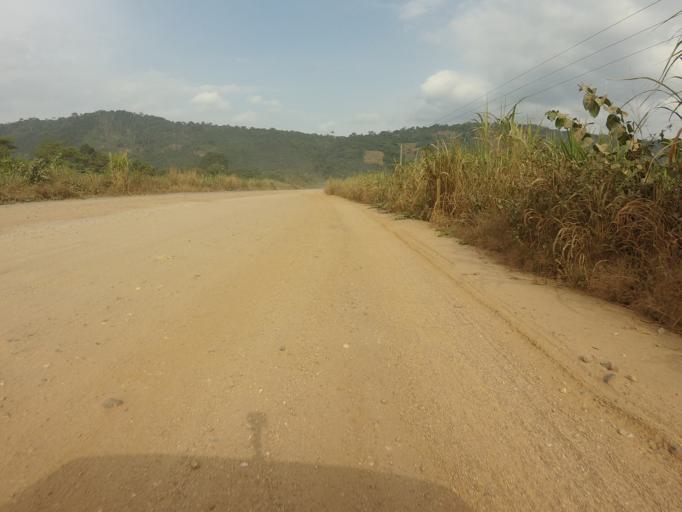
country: GH
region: Volta
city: Ho
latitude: 6.6321
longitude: 0.3071
